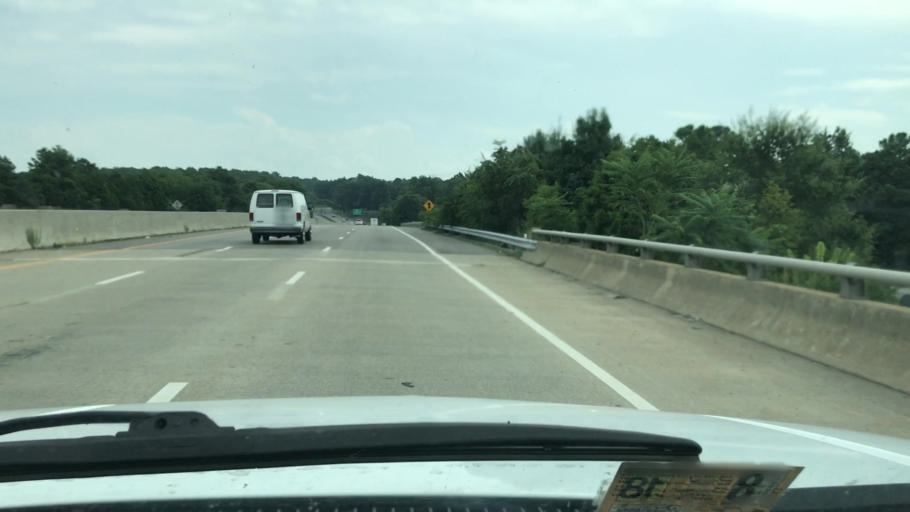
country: US
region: Virginia
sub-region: Chesterfield County
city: Bon Air
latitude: 37.4786
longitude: -77.5154
